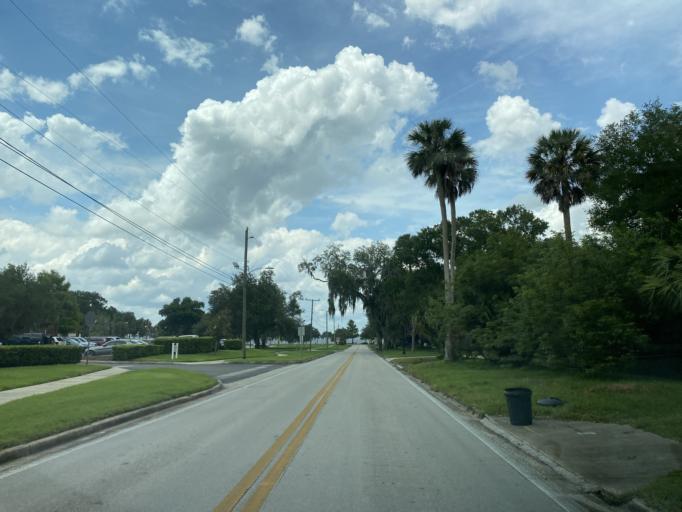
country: US
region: Florida
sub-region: Seminole County
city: Sanford
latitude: 28.8103
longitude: -81.2549
